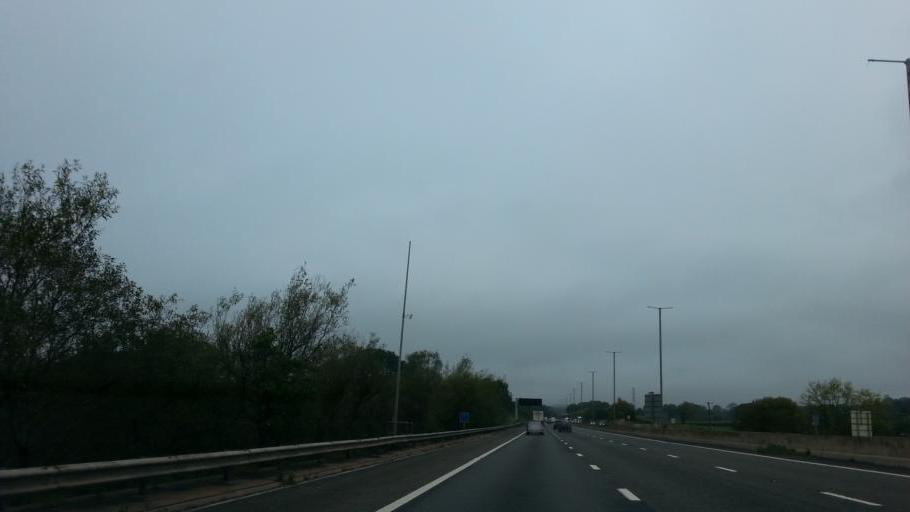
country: GB
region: England
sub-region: Worcestershire
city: Barnt Green
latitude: 52.3848
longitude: -2.0480
